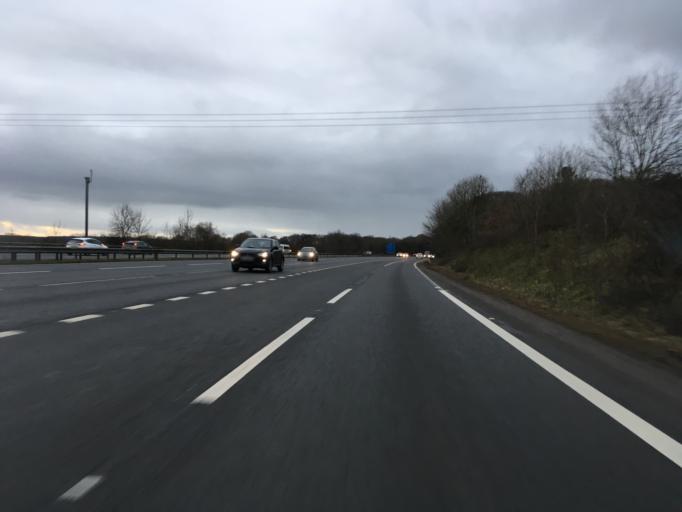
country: GB
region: Wales
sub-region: Cardiff
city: Pentyrch
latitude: 51.5061
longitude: -3.3170
